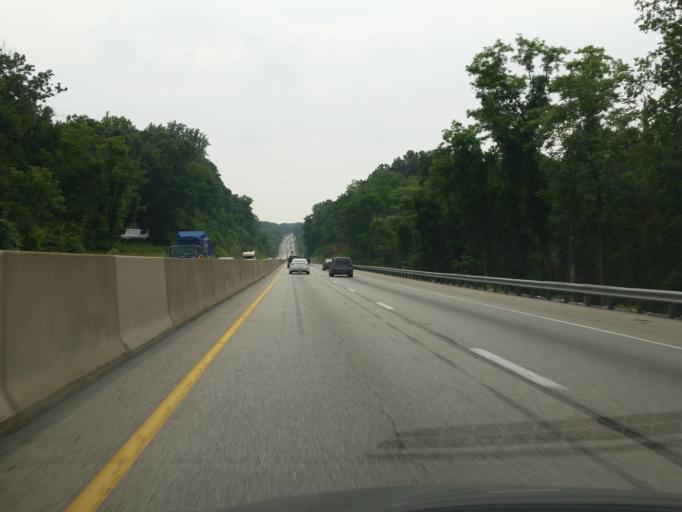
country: US
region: Pennsylvania
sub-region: York County
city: Valley Green
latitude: 40.0969
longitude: -76.7747
